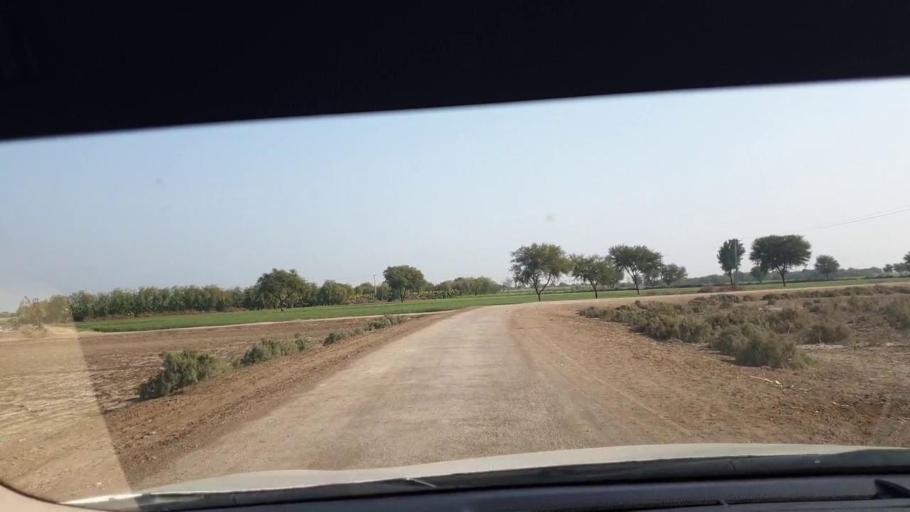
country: PK
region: Sindh
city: Berani
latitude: 25.8179
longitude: 68.7755
